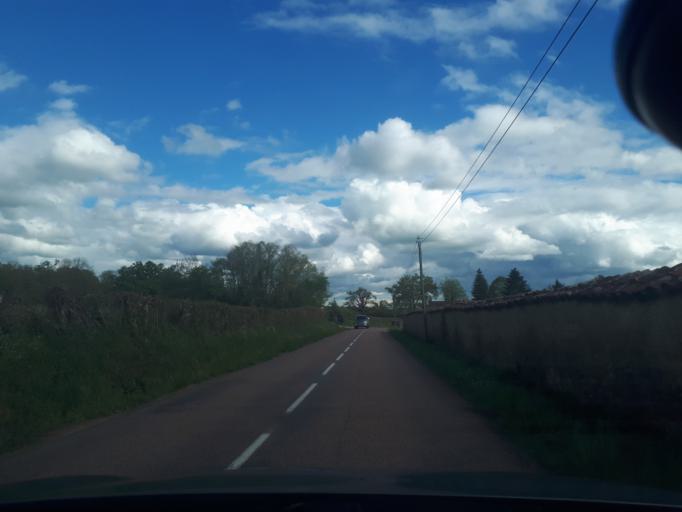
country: FR
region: Rhone-Alpes
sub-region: Departement de la Loire
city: Pouilly-les-Feurs
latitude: 45.8065
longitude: 4.2238
